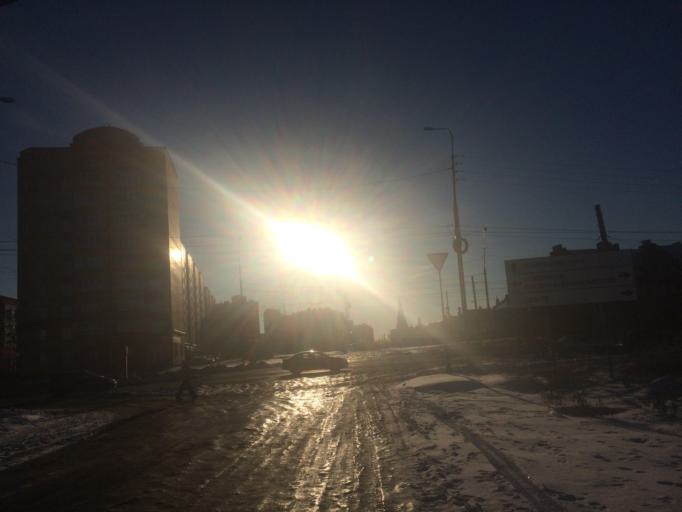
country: RU
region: Mariy-El
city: Yoshkar-Ola
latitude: 56.6372
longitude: 47.9152
